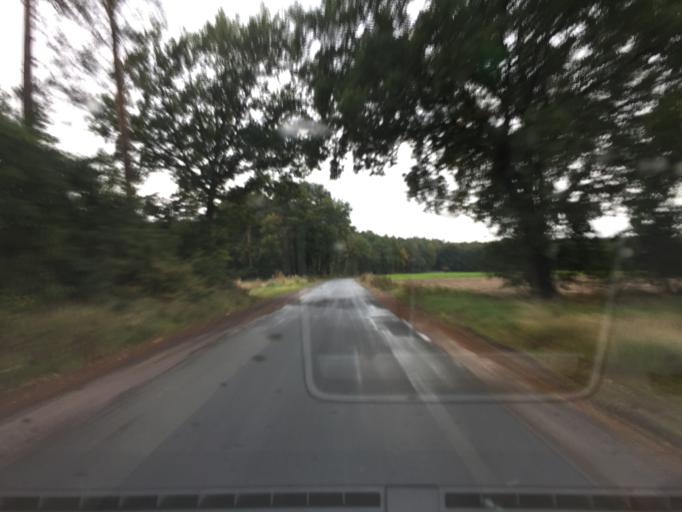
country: DE
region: Lower Saxony
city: Liebenau
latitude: 52.6273
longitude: 9.0979
